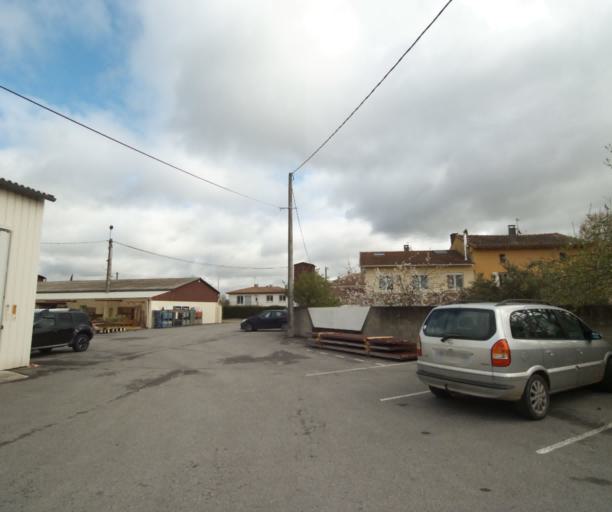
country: FR
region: Midi-Pyrenees
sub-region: Departement de l'Ariege
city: Saverdun
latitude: 43.2410
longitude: 1.5672
